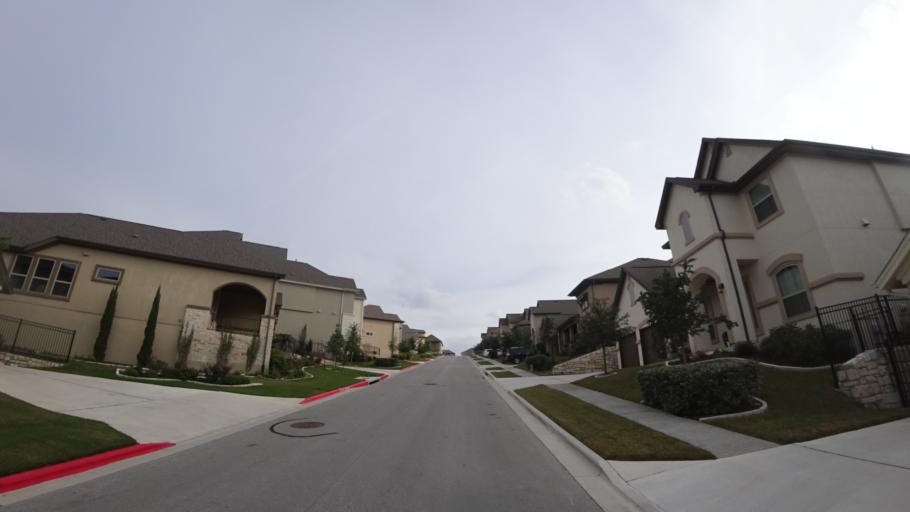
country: US
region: Texas
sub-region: Travis County
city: Hudson Bend
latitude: 30.3798
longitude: -97.8808
